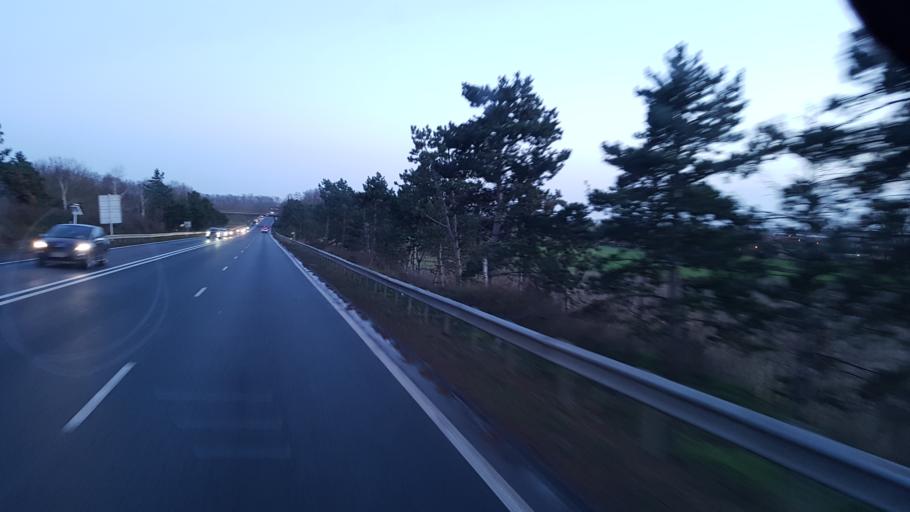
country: FR
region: Nord-Pas-de-Calais
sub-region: Departement du Nord
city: Lambres-lez-Douai
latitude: 50.3477
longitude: 3.0673
